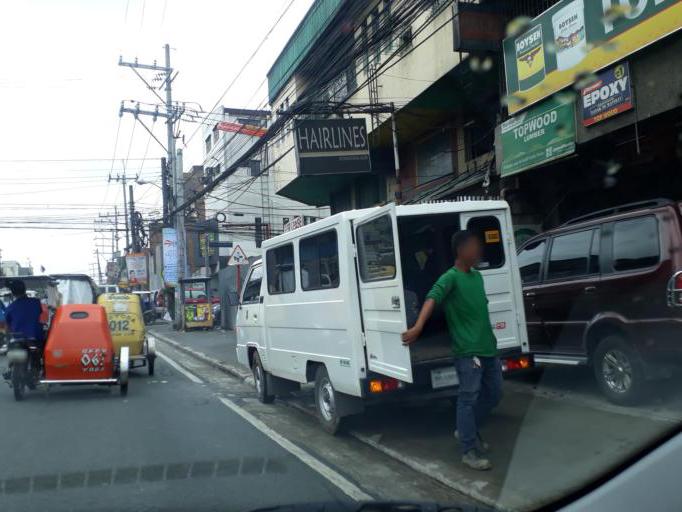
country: PH
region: Calabarzon
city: Del Monte
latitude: 14.6535
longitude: 121.0183
